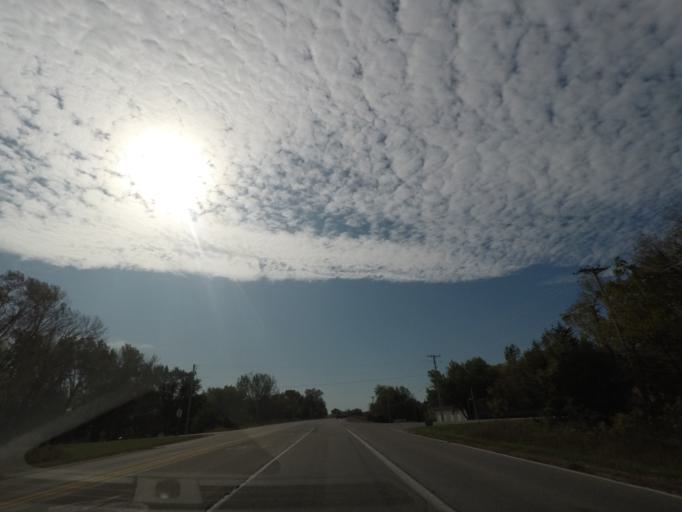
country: US
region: Iowa
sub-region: Story County
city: Gilbert
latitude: 42.0784
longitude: -93.6207
